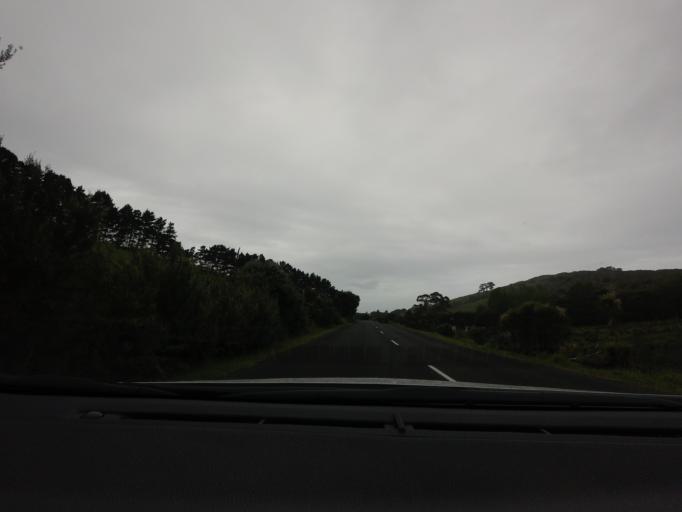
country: NZ
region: Auckland
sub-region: Auckland
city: Warkworth
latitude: -36.2755
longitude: 174.7928
